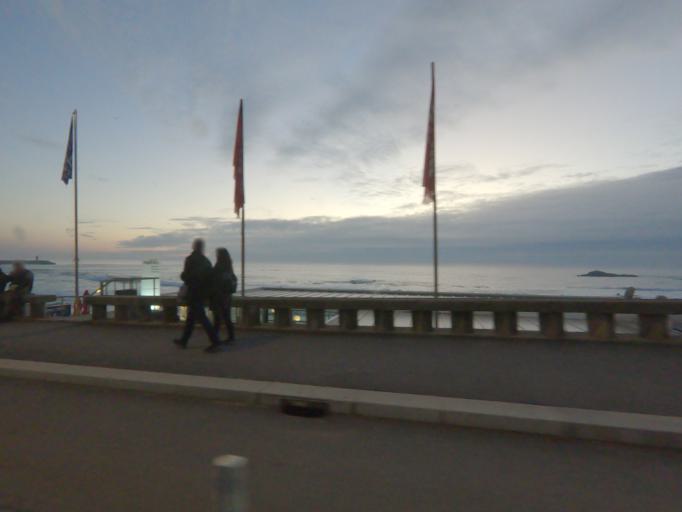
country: PT
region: Porto
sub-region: Matosinhos
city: Matosinhos
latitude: 41.1524
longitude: -8.6783
